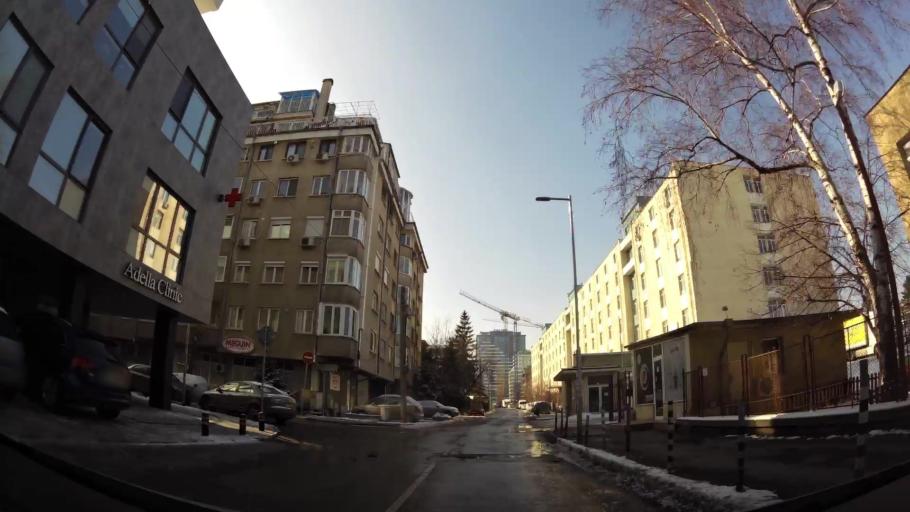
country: BG
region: Sofia-Capital
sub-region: Stolichna Obshtina
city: Sofia
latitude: 42.6670
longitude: 23.3498
